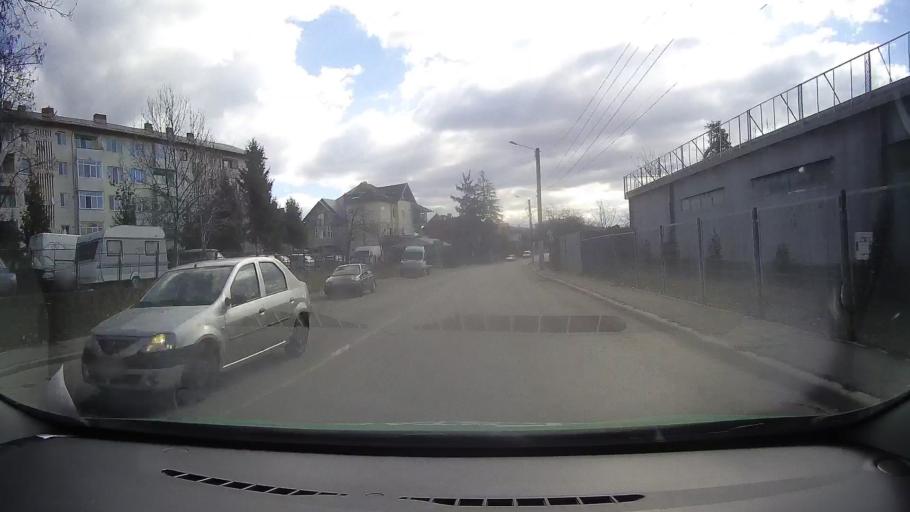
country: RO
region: Dambovita
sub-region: Oras Pucioasa
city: Pucioasa
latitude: 45.0763
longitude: 25.4310
